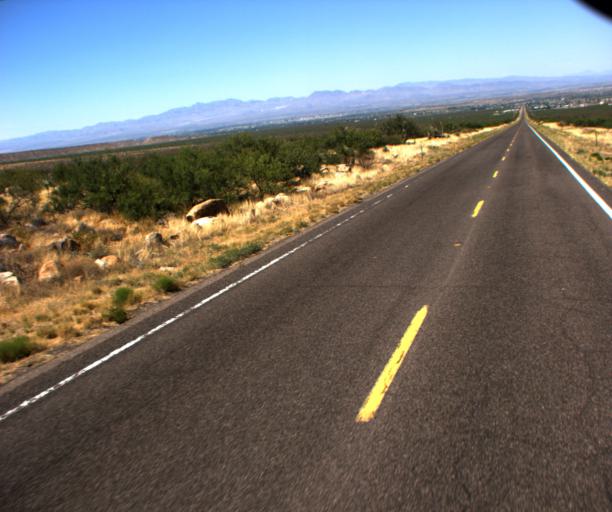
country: US
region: Arizona
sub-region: Graham County
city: Swift Trail Junction
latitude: 32.6951
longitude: -109.7491
